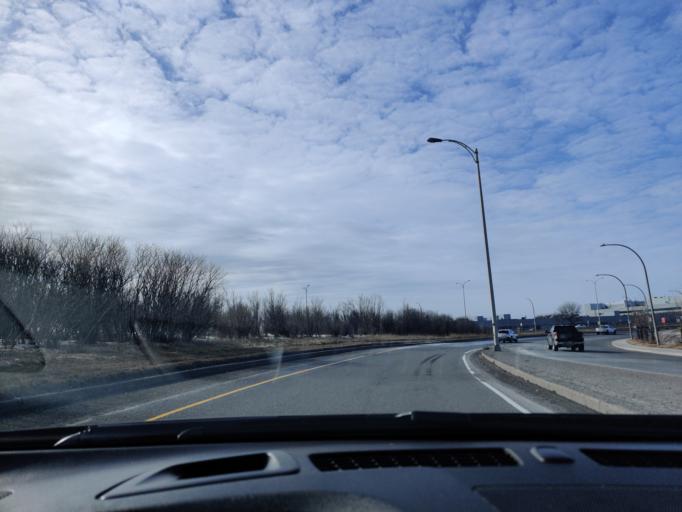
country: CA
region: Quebec
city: Dorval
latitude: 45.4919
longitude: -73.7414
